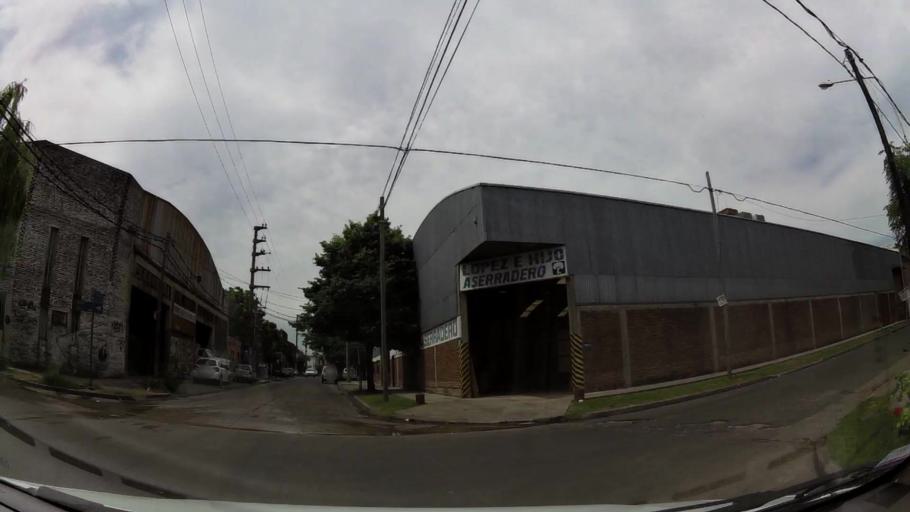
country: AR
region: Buenos Aires
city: San Justo
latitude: -34.6724
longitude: -58.5322
